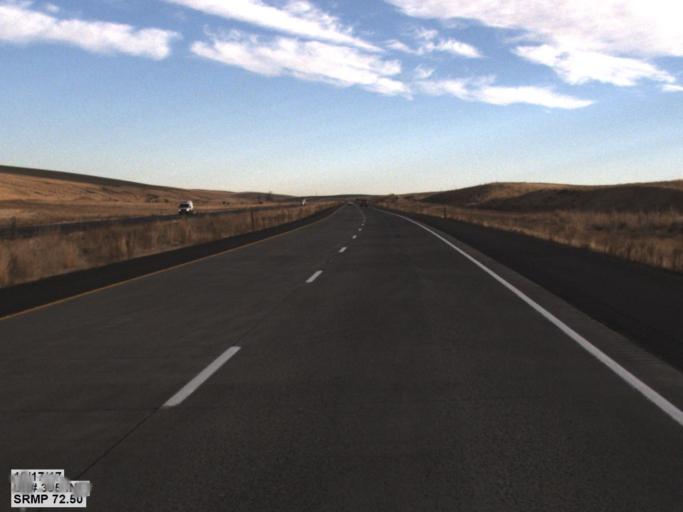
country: US
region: Washington
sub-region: Franklin County
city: Connell
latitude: 46.8418
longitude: -118.6456
